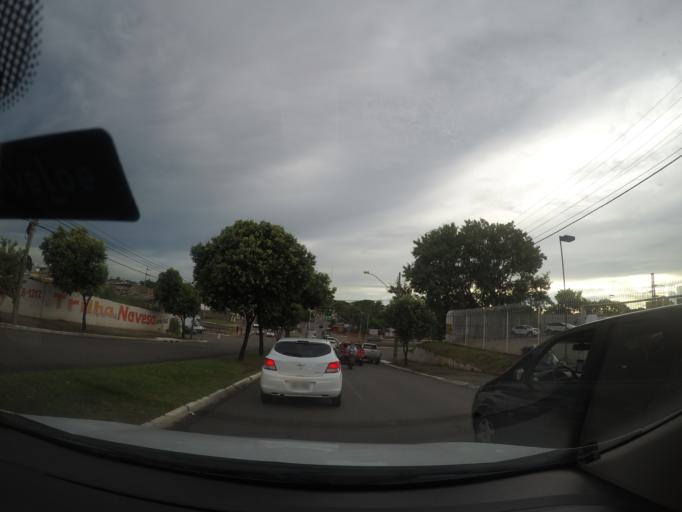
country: BR
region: Goias
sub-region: Goiania
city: Goiania
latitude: -16.6756
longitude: -49.2953
